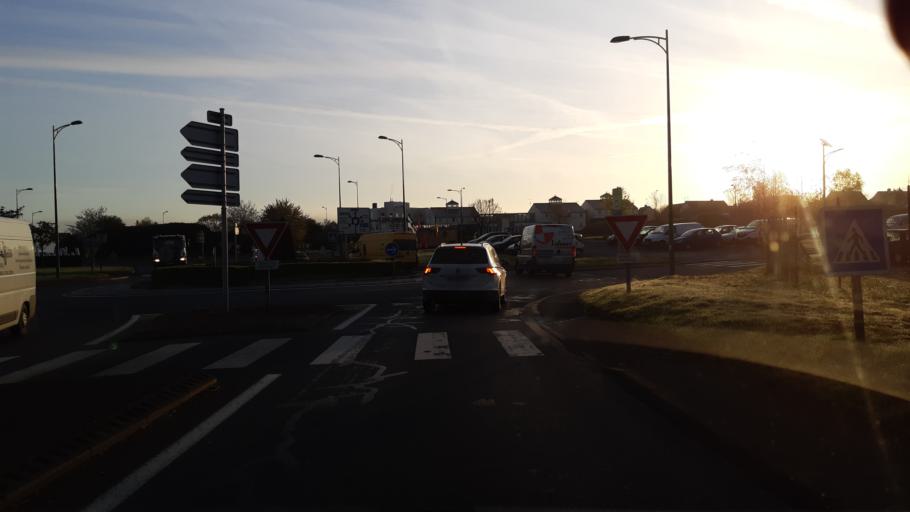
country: FR
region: Lower Normandy
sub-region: Departement de la Manche
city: Agneaux
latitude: 49.1003
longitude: -1.1172
